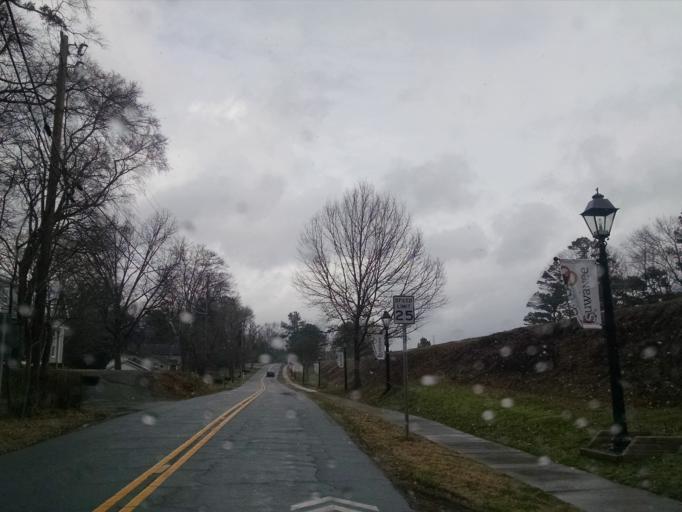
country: US
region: Georgia
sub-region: Gwinnett County
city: Suwanee
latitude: 34.0532
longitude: -84.0715
